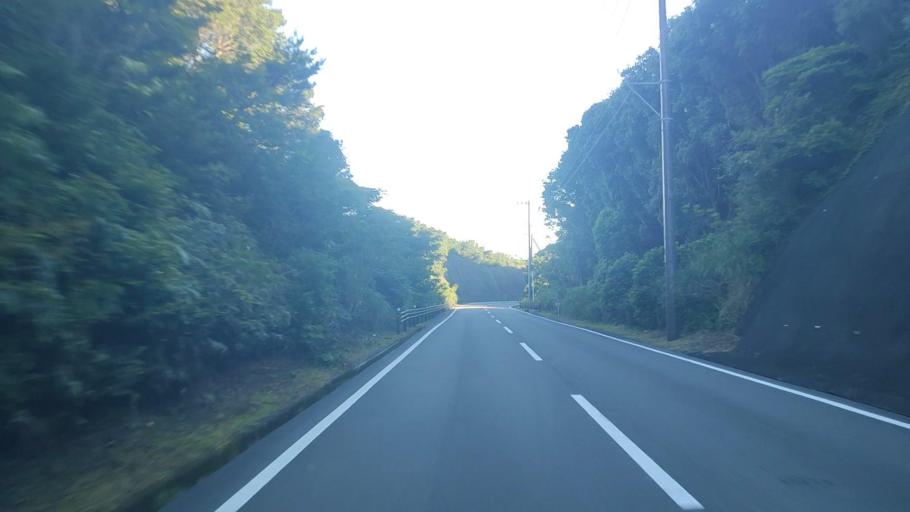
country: JP
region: Mie
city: Toba
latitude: 34.4026
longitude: 136.8808
